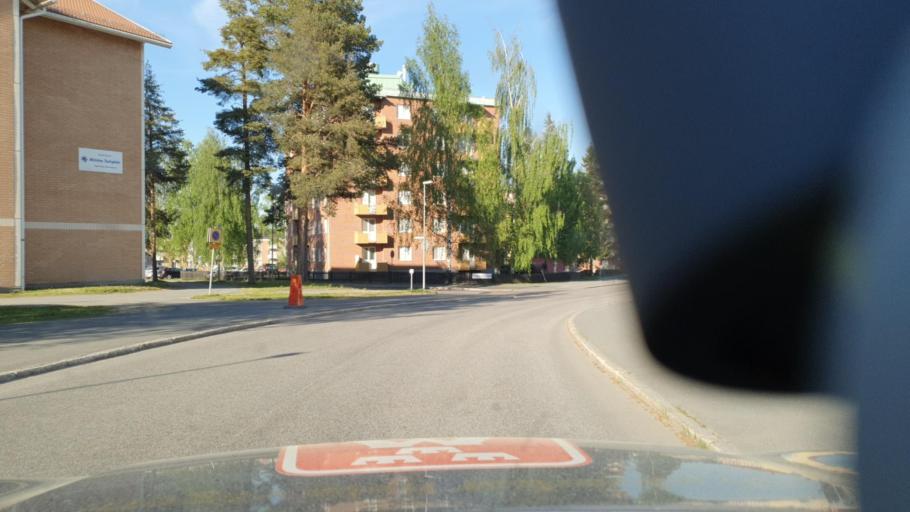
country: SE
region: Norrbotten
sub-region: Bodens Kommun
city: Boden
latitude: 65.8190
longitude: 21.6665
